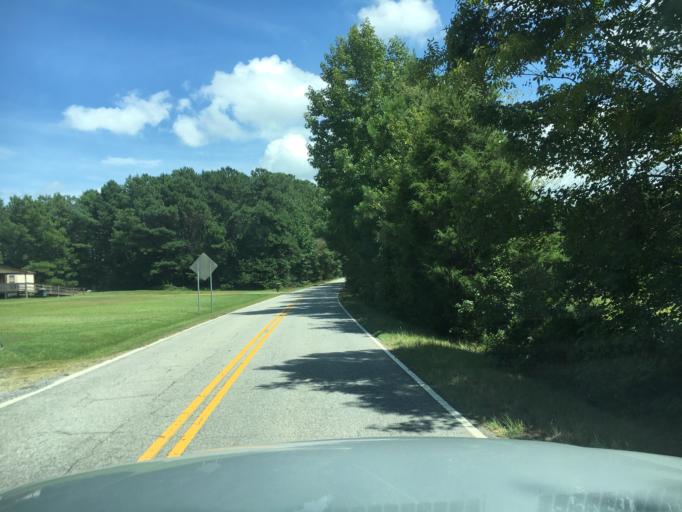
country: US
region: South Carolina
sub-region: Anderson County
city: Belton
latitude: 34.5711
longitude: -82.4915
